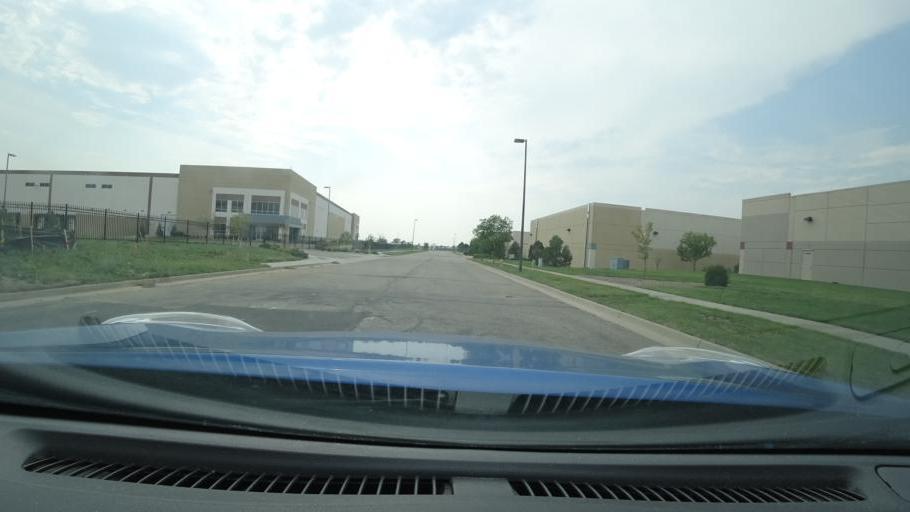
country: US
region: Colorado
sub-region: Adams County
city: Aurora
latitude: 39.7516
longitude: -104.7580
